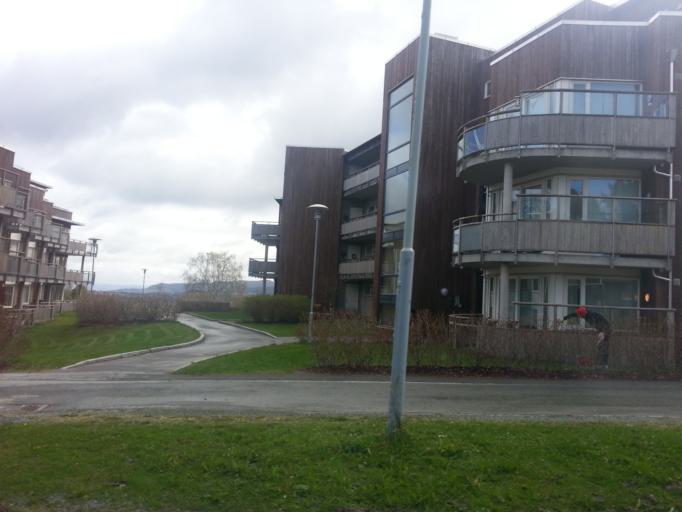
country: NO
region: Sor-Trondelag
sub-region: Trondheim
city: Trondheim
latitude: 63.4111
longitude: 10.3511
